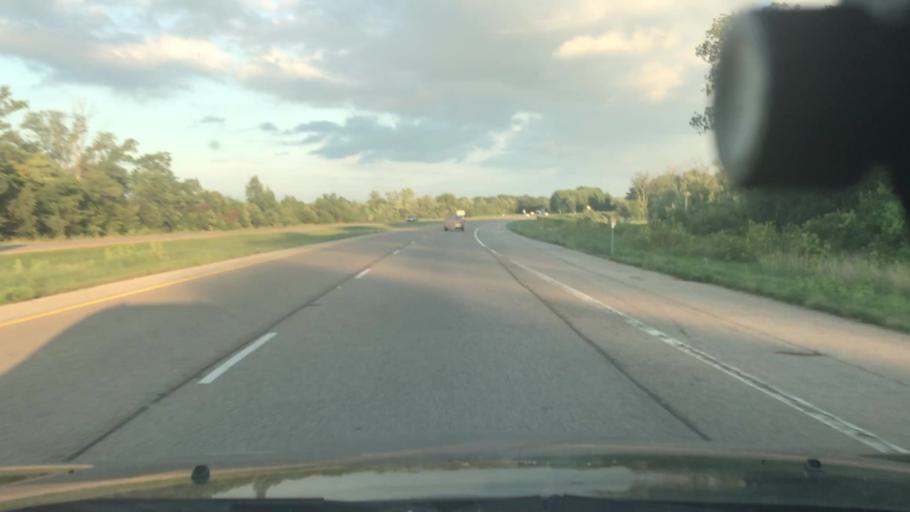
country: US
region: Illinois
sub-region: Clinton County
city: Albers
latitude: 38.4974
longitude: -89.6053
